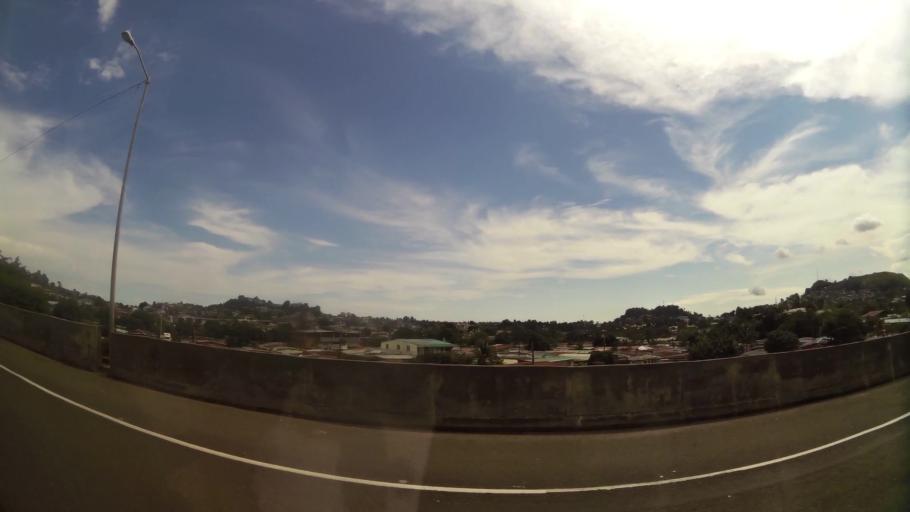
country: PA
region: Panama
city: San Miguelito
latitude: 9.0717
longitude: -79.4911
